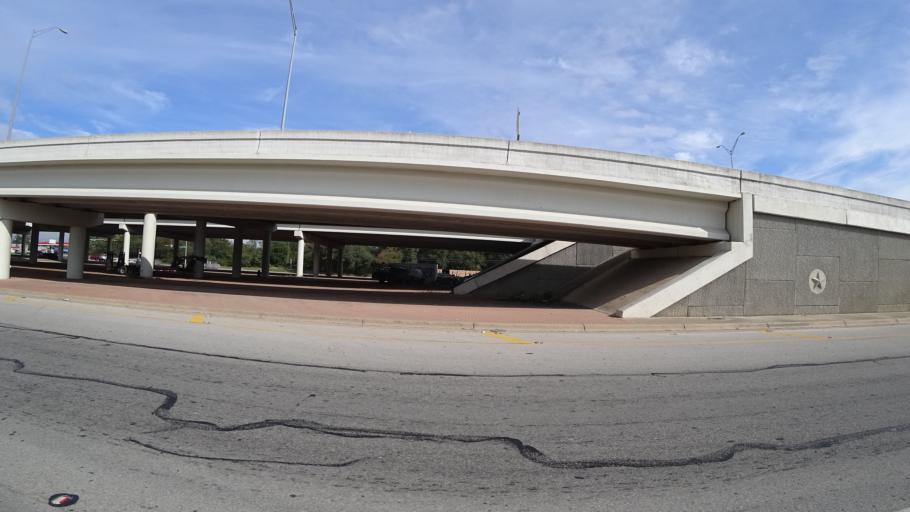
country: US
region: Texas
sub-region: Travis County
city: Austin
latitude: 30.2145
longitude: -97.7325
